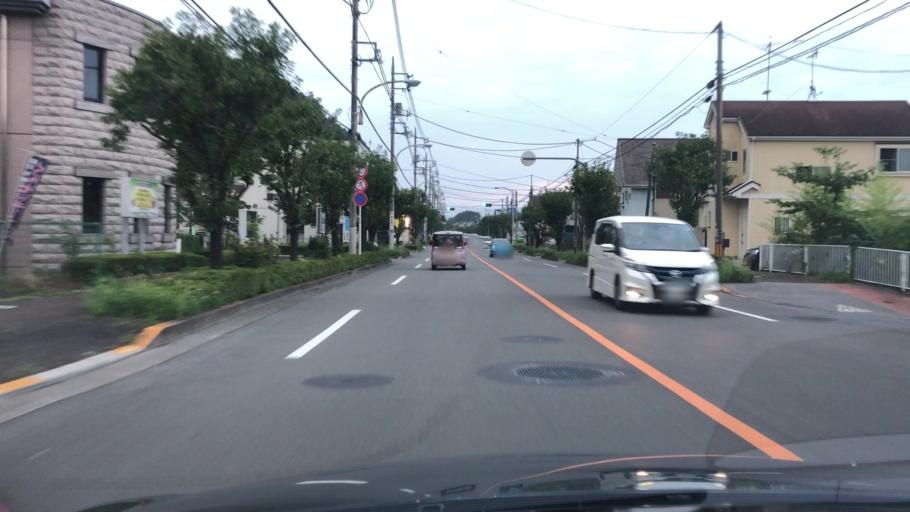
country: JP
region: Tokyo
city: Ome
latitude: 35.7424
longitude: 139.2589
